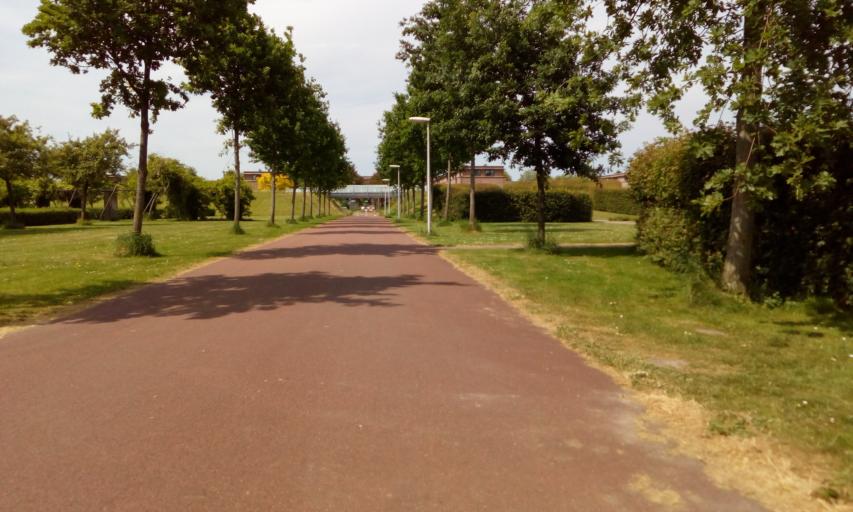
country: NL
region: South Holland
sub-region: Gemeente Zoetermeer
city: Zoetermeer
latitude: 52.0425
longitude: 4.4680
